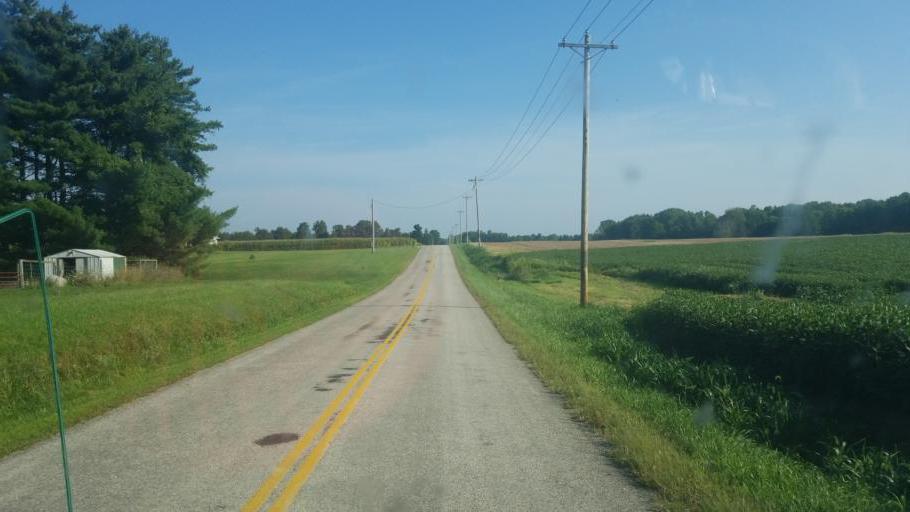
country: US
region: Ohio
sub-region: Huron County
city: New London
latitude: 41.0313
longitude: -82.3565
